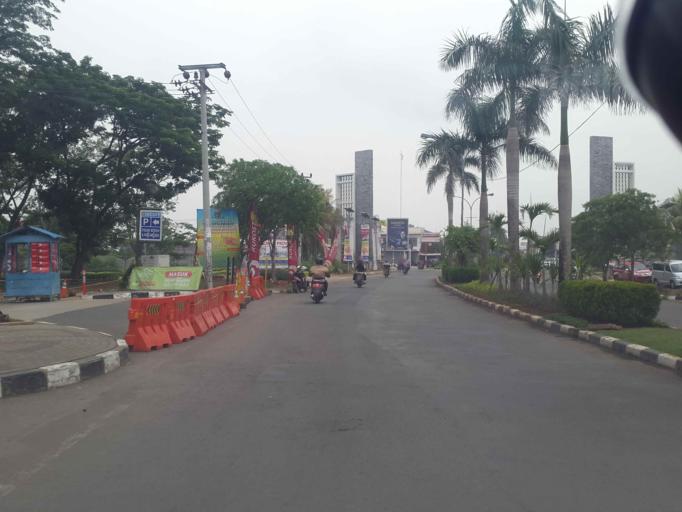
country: ID
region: West Java
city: Cikarang
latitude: -6.3198
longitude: 107.2920
